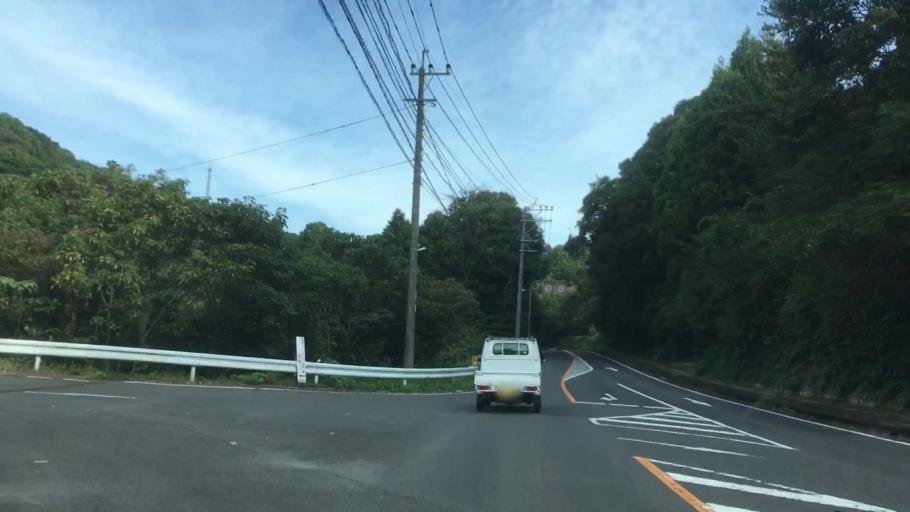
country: JP
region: Nagasaki
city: Sasebo
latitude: 33.0265
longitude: 129.6534
